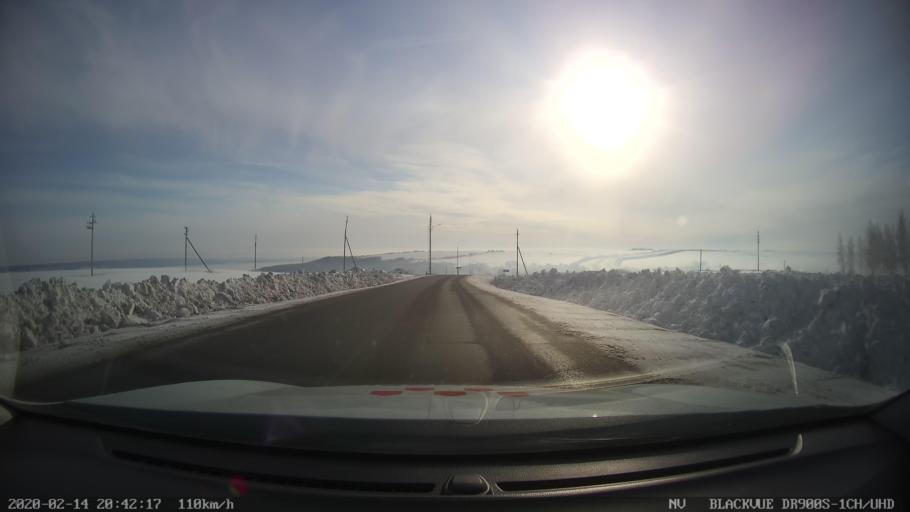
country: RU
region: Tatarstan
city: Kuybyshevskiy Zaton
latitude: 55.3186
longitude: 49.1403
